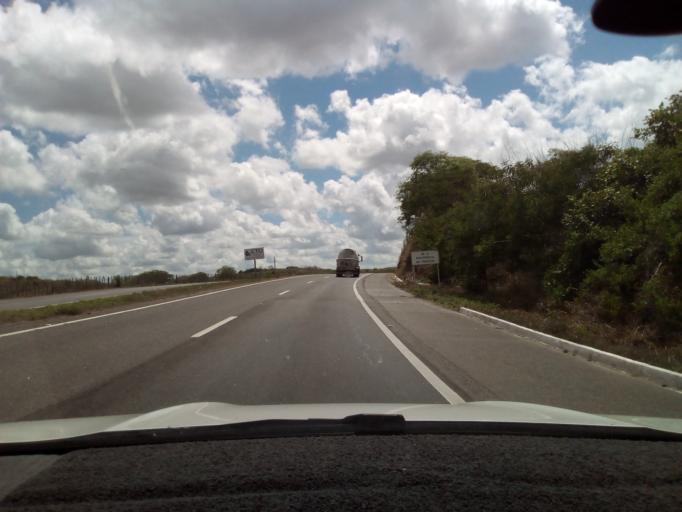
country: BR
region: Paraiba
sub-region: Massaranduba
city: Massaranduba
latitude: -7.2657
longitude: -35.7186
